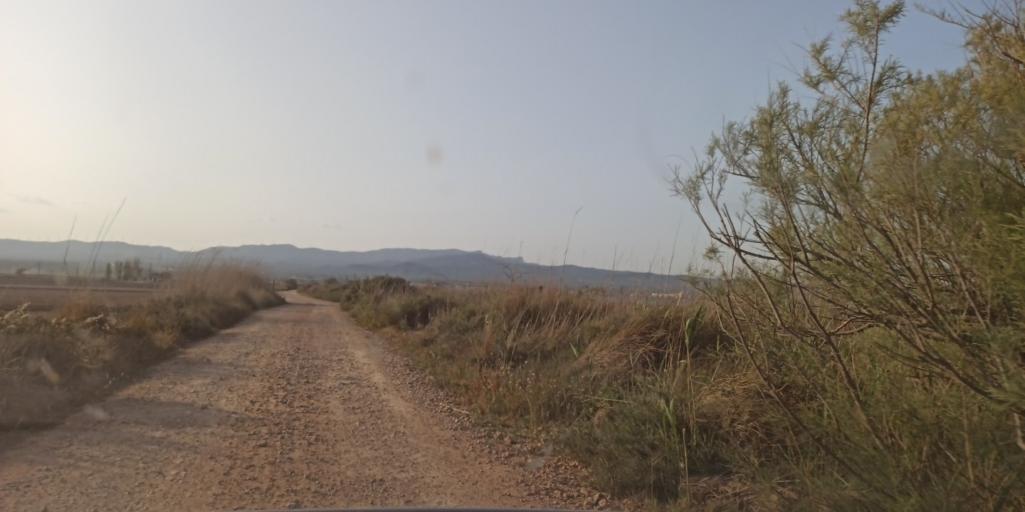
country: ES
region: Catalonia
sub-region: Provincia de Tarragona
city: L'Ampolla
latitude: 40.7797
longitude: 0.7167
